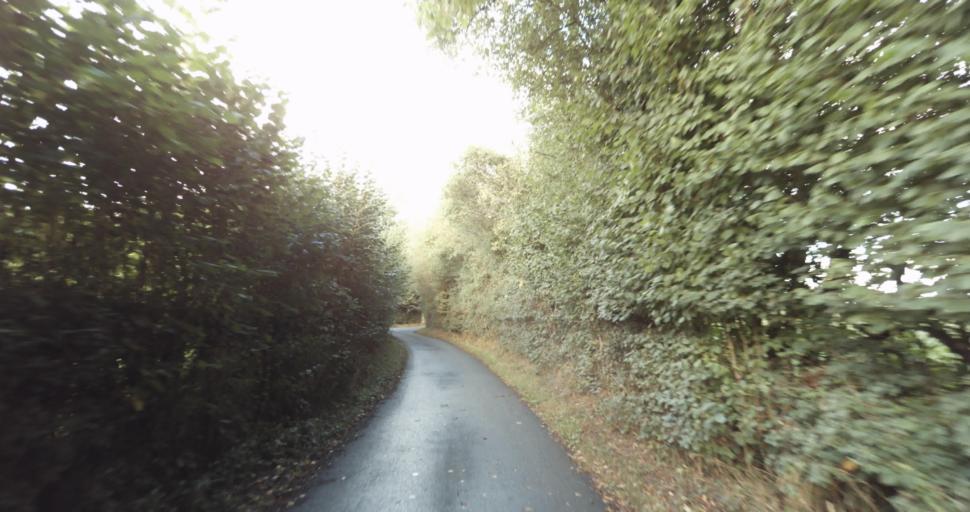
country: FR
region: Lower Normandy
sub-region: Departement de l'Orne
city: Sainte-Gauburge-Sainte-Colombe
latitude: 48.7292
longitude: 0.4130
